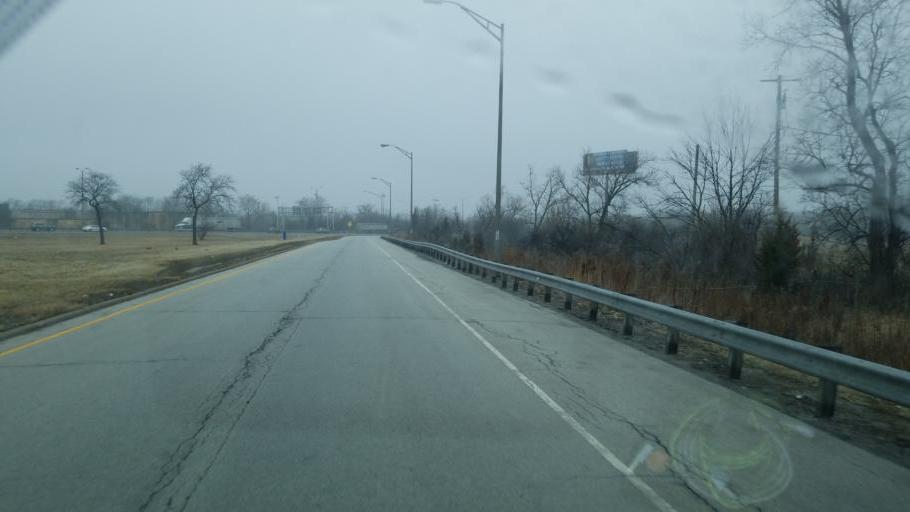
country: US
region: Illinois
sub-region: Cook County
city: South Holland
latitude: 41.6021
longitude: -87.5816
